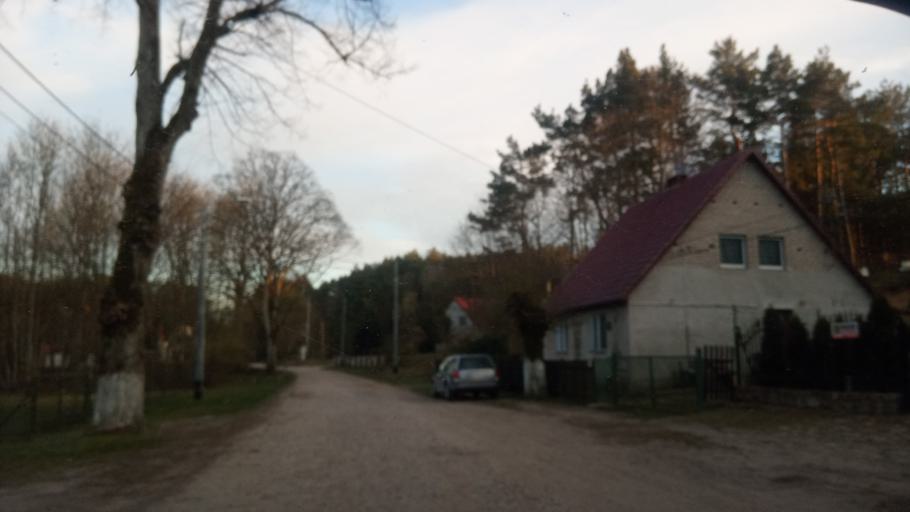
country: PL
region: West Pomeranian Voivodeship
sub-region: Powiat szczecinecki
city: Lubowo
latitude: 53.5485
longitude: 16.3966
